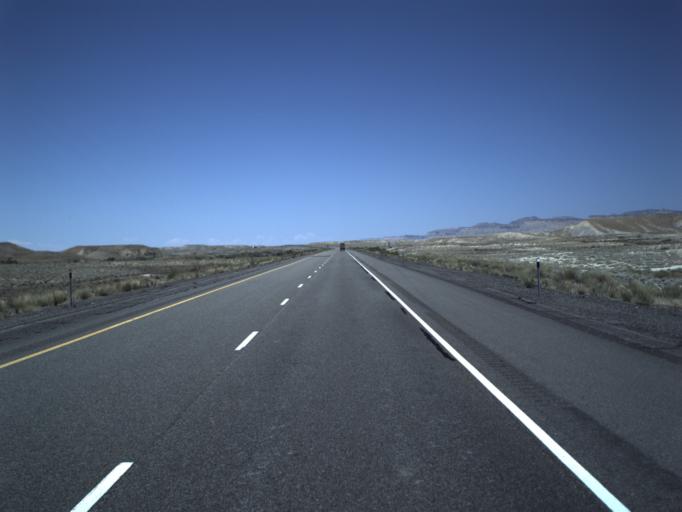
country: US
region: Utah
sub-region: Grand County
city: Moab
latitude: 38.9407
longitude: -109.5094
